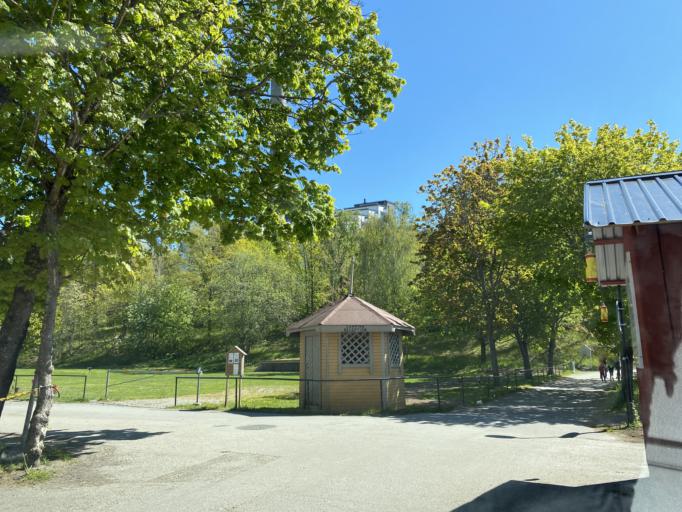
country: SE
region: Stockholm
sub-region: Stockholms Kommun
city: Bromma
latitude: 59.3072
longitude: 17.9607
